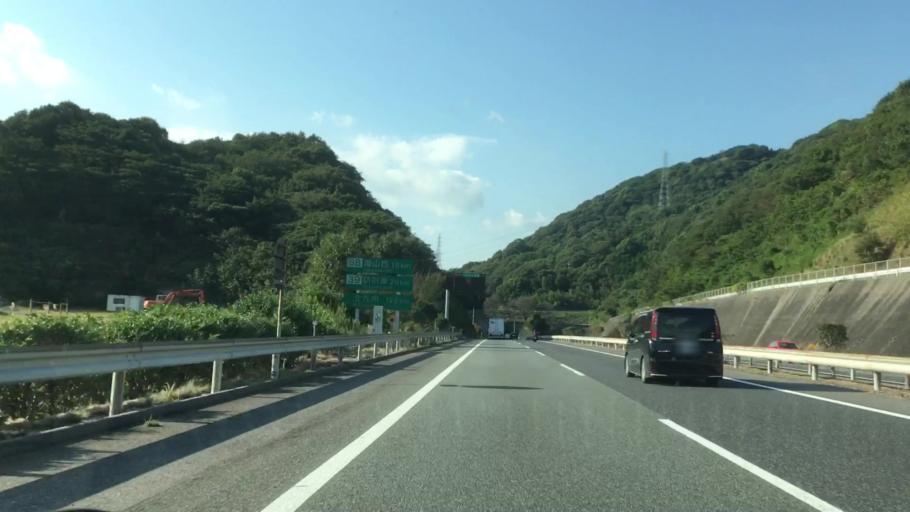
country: JP
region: Yamaguchi
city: Tokuyama
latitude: 34.0580
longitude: 131.8380
